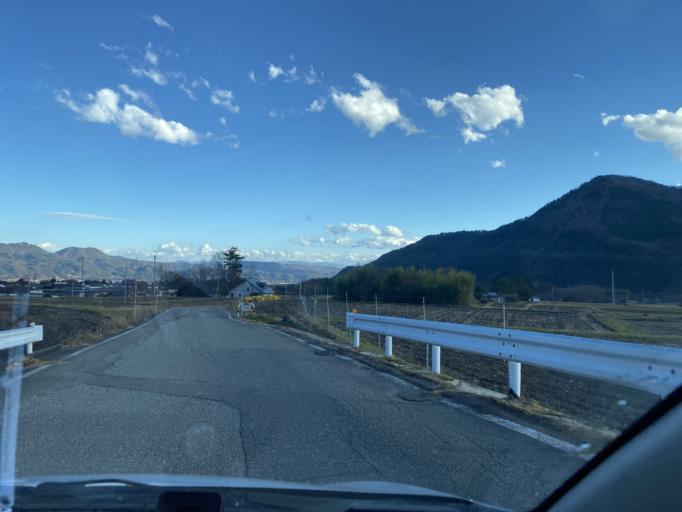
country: JP
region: Nagano
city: Omachi
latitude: 36.5216
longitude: 137.8009
